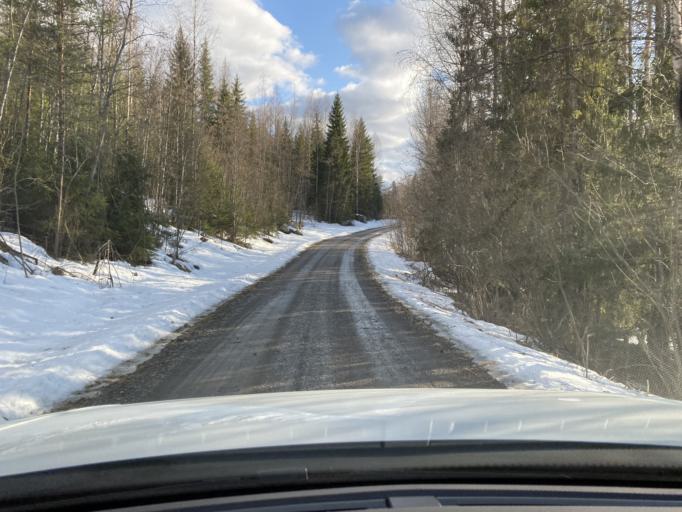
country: FI
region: Pirkanmaa
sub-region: Lounais-Pirkanmaa
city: Mouhijaervi
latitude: 61.4534
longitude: 22.9599
